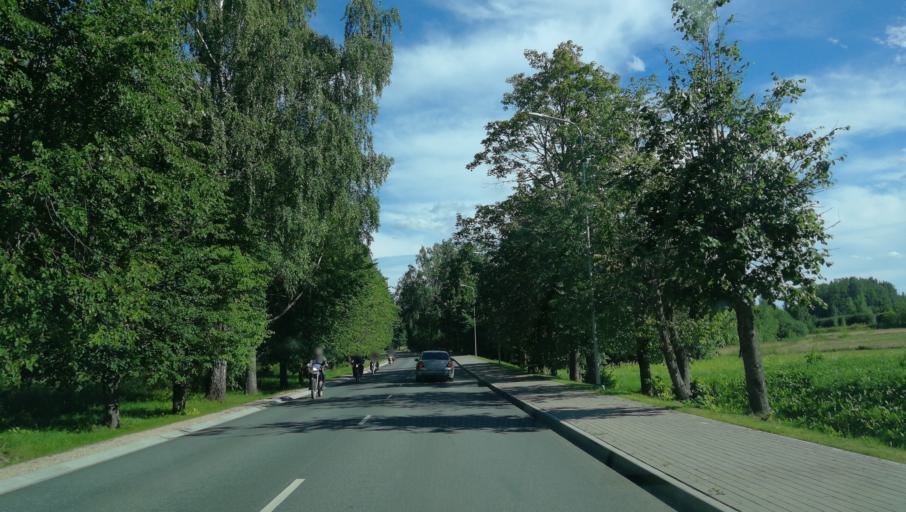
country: LV
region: Cesvaine
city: Cesvaine
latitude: 56.9668
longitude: 26.3179
